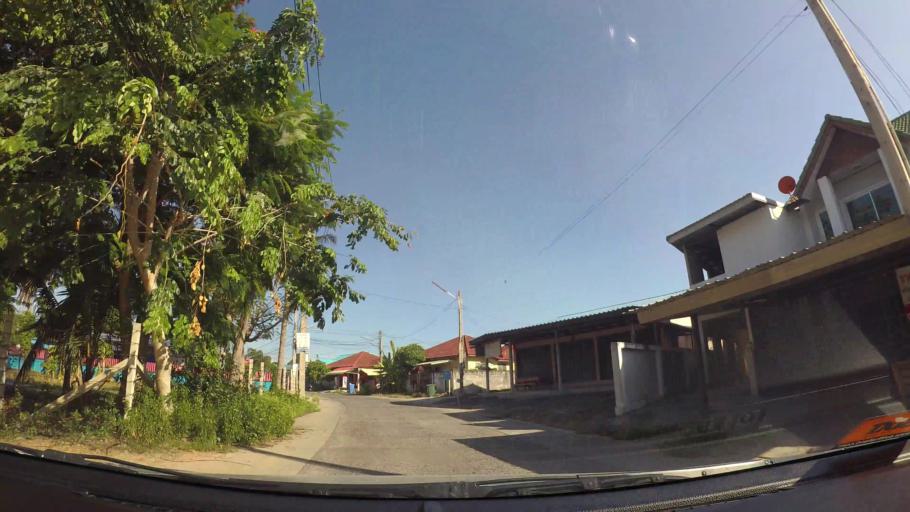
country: TH
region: Chon Buri
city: Si Racha
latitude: 13.1518
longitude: 100.9392
